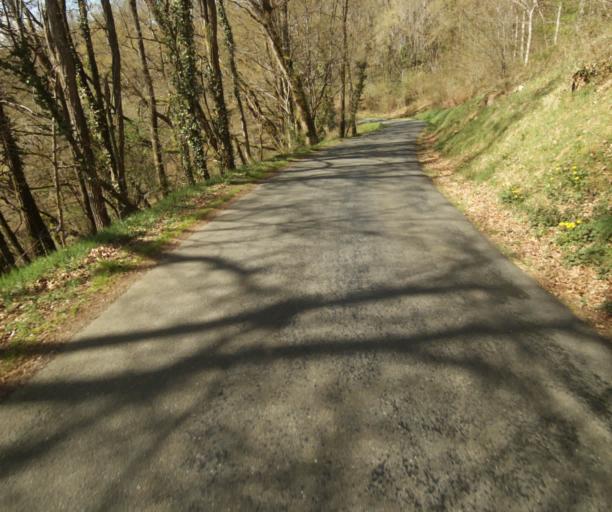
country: FR
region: Limousin
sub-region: Departement de la Correze
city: Naves
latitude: 45.3446
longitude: 1.7810
